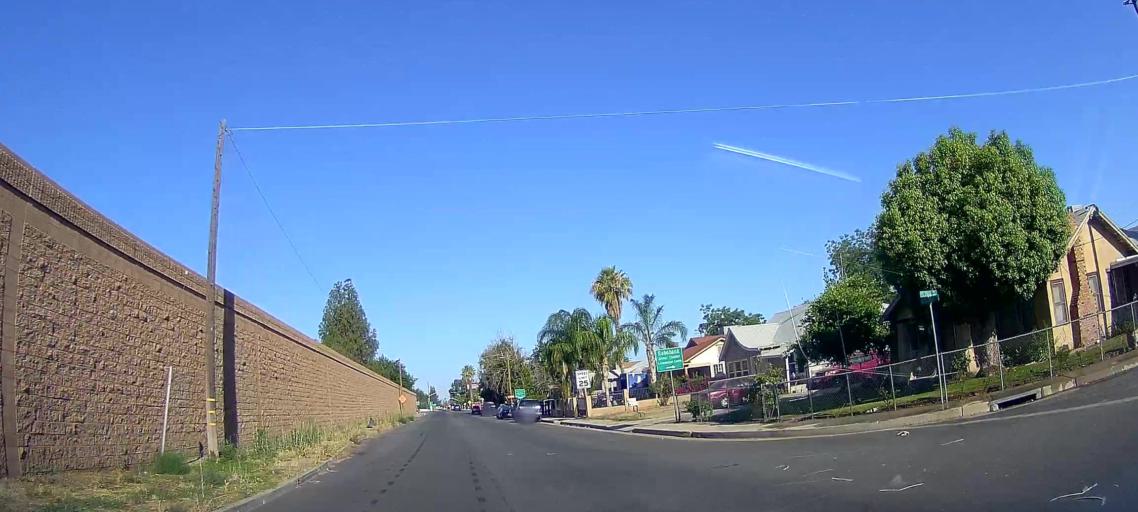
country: US
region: California
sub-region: Kern County
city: Bakersfield
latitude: 35.3530
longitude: -119.0172
